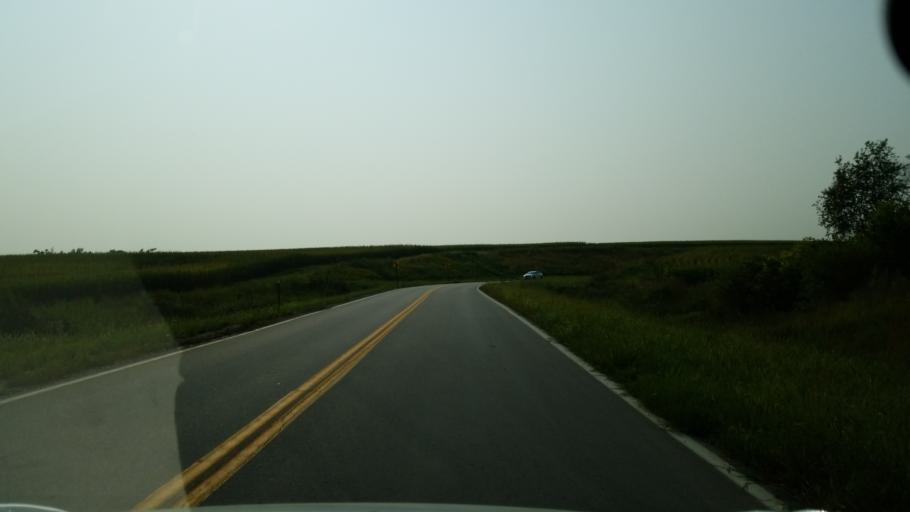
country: US
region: Nebraska
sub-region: Sarpy County
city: Offutt Air Force Base
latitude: 41.0804
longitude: -95.9334
